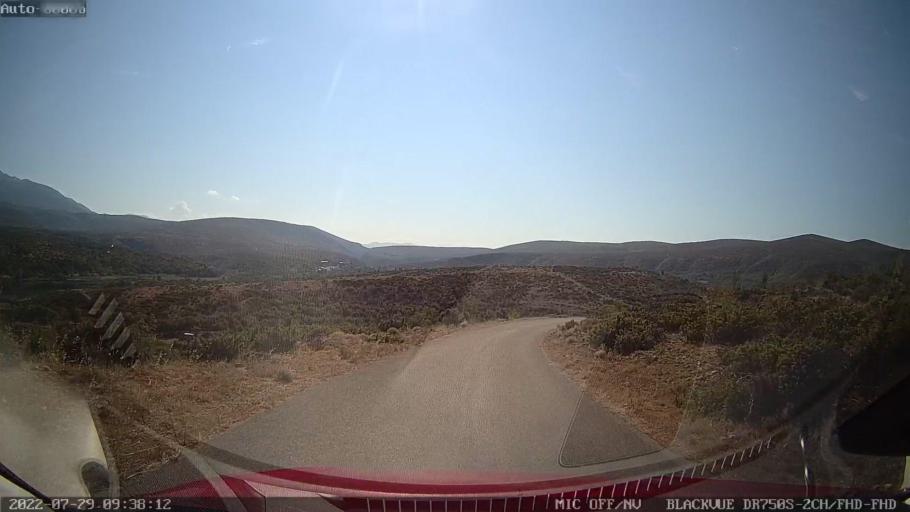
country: HR
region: Zadarska
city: Obrovac
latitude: 44.1999
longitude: 15.7482
